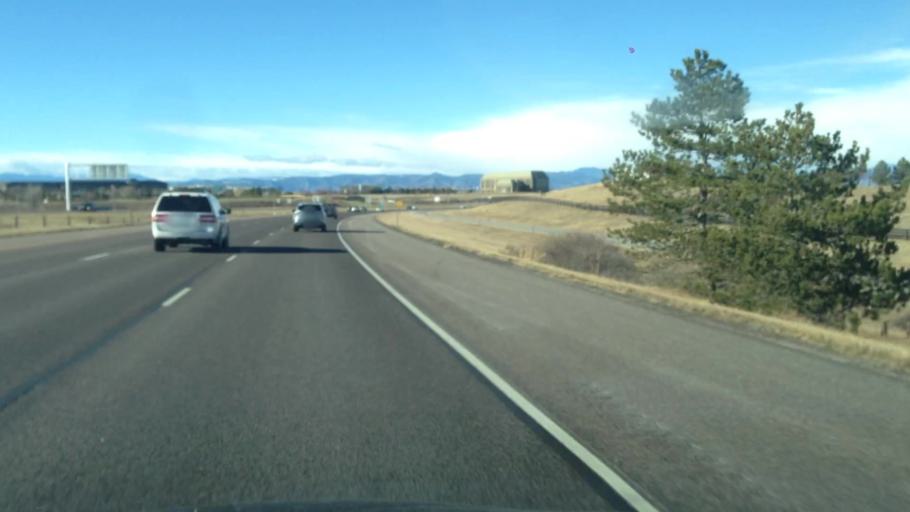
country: US
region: Colorado
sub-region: Douglas County
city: Meridian
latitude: 39.5517
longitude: -104.8418
